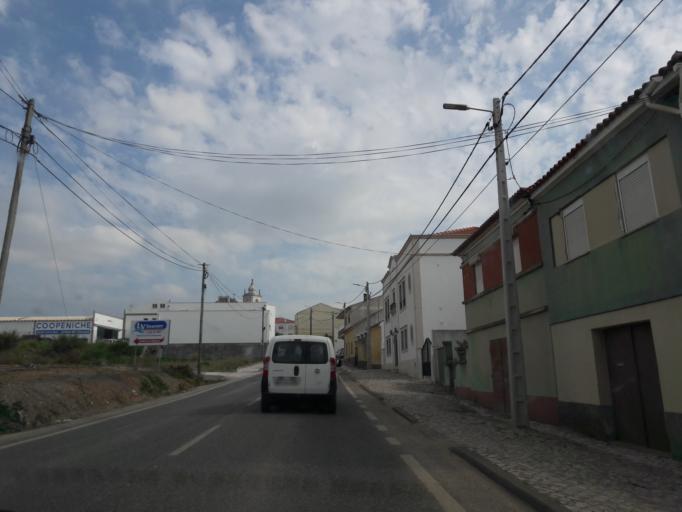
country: PT
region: Leiria
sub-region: Peniche
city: Atouguia da Baleia
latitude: 39.3414
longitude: -9.3276
